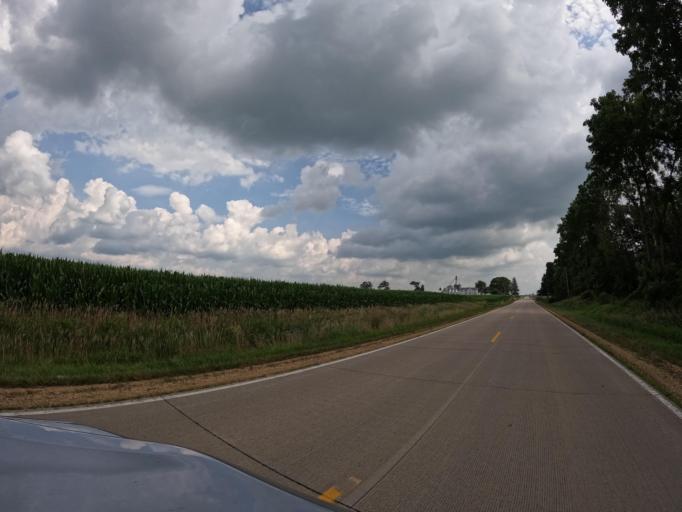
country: US
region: Iowa
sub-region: Clinton County
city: De Witt
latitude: 41.7994
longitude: -90.4133
